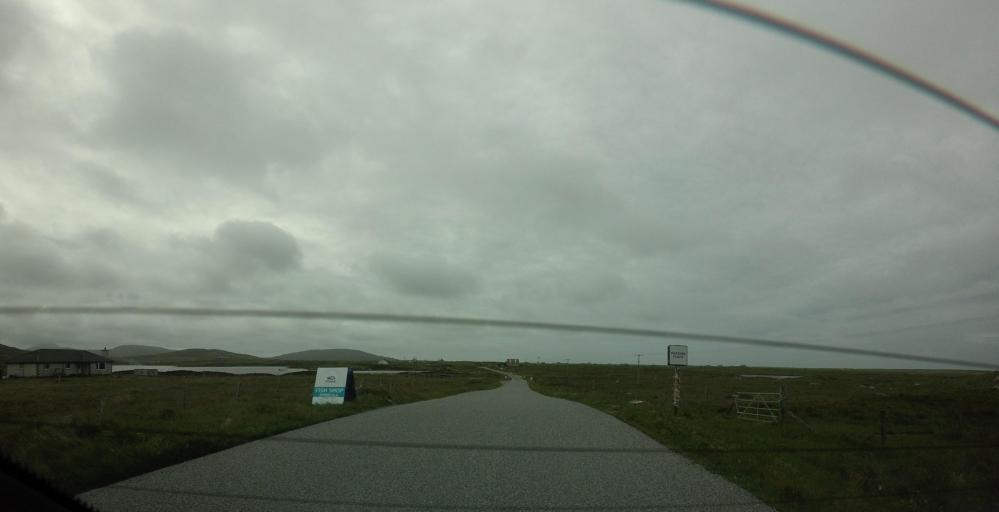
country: GB
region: Scotland
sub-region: Eilean Siar
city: Isle of South Uist
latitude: 57.2217
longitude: -7.3965
